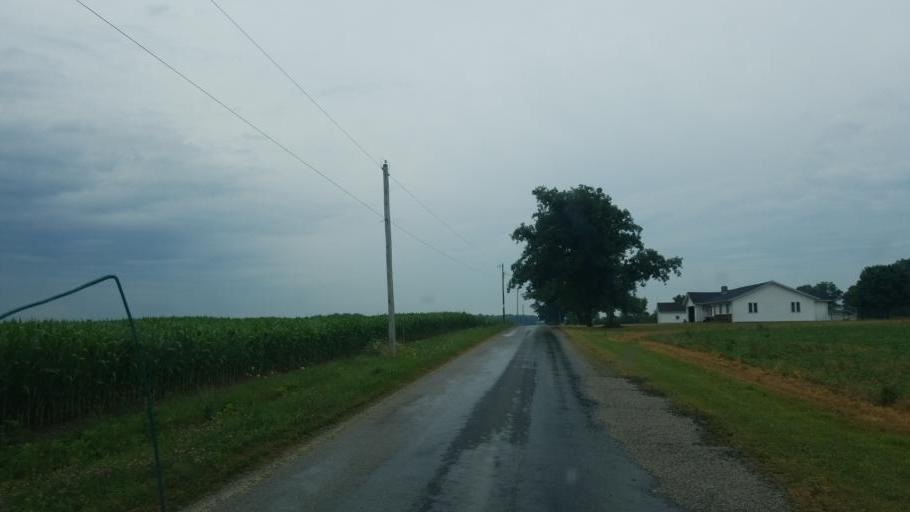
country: US
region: Ohio
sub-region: Williams County
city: Edgerton
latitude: 41.4201
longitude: -84.6703
